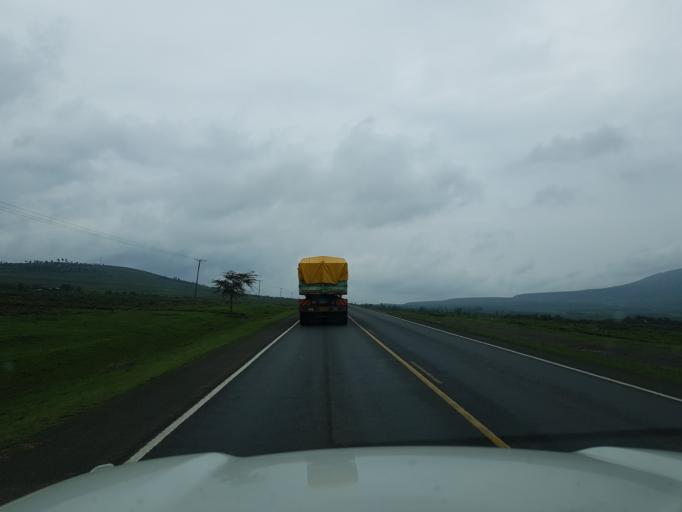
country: KE
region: Nakuru
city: Kijabe
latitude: -0.8604
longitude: 36.4808
